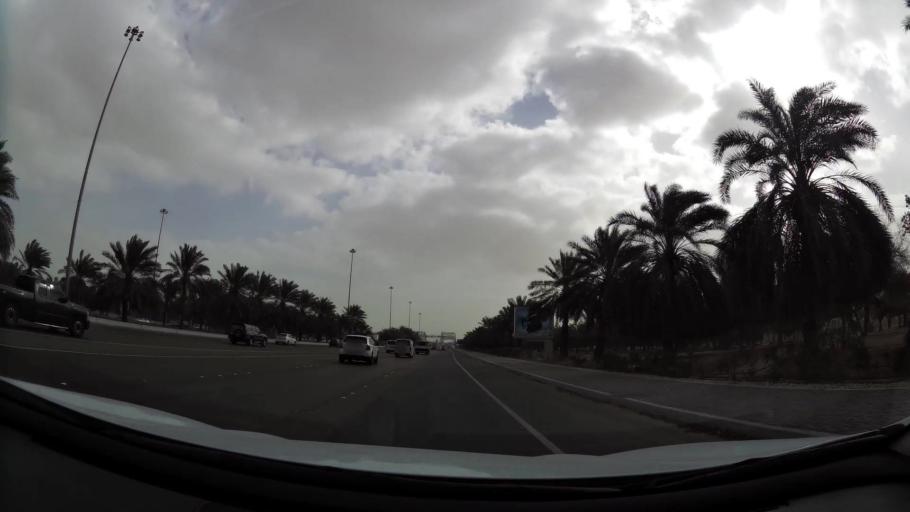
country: AE
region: Abu Dhabi
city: Abu Dhabi
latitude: 24.4195
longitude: 54.4804
